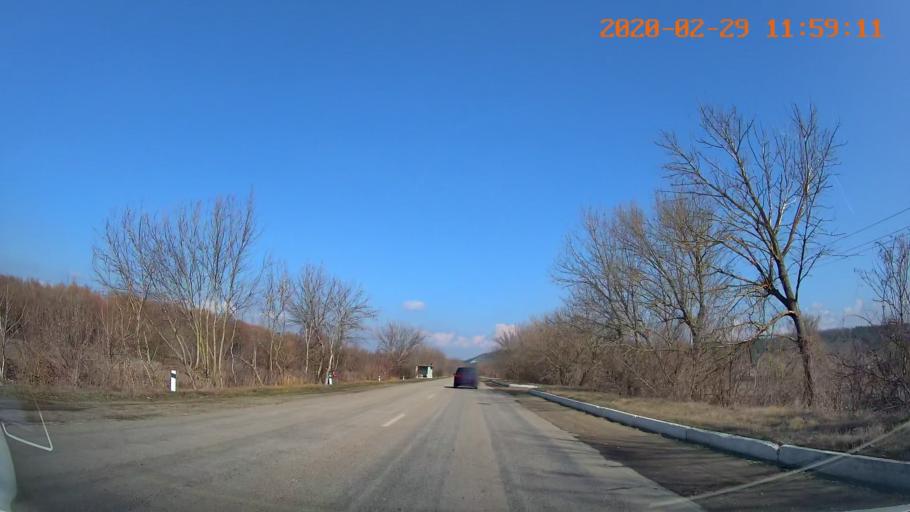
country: MD
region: Telenesti
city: Ribnita
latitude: 47.8222
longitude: 29.0155
